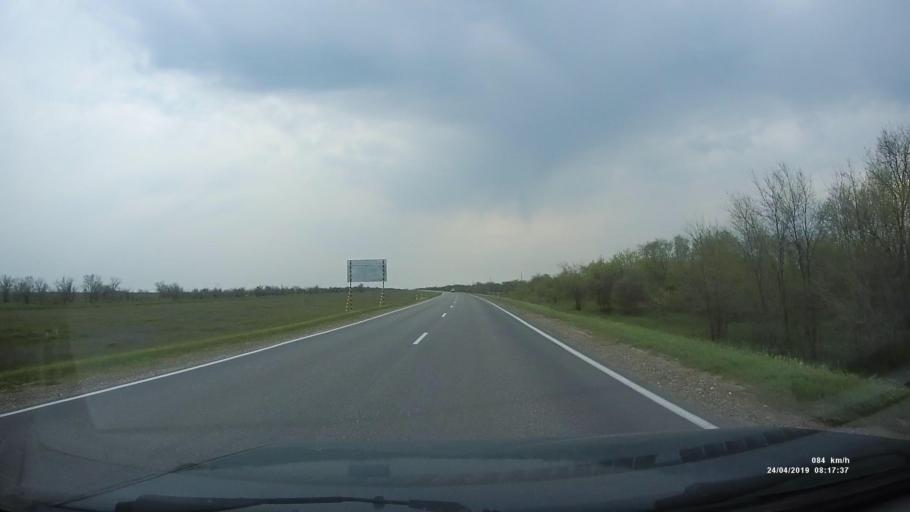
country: RU
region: Kalmykiya
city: Priyutnoye
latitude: 46.0968
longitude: 43.6342
